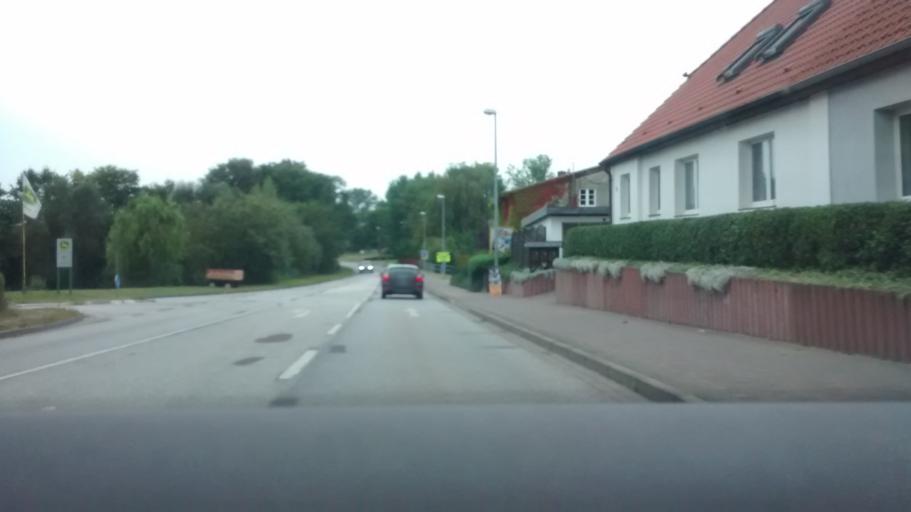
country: DE
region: Mecklenburg-Vorpommern
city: Mecklenburg
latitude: 53.8411
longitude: 11.4589
